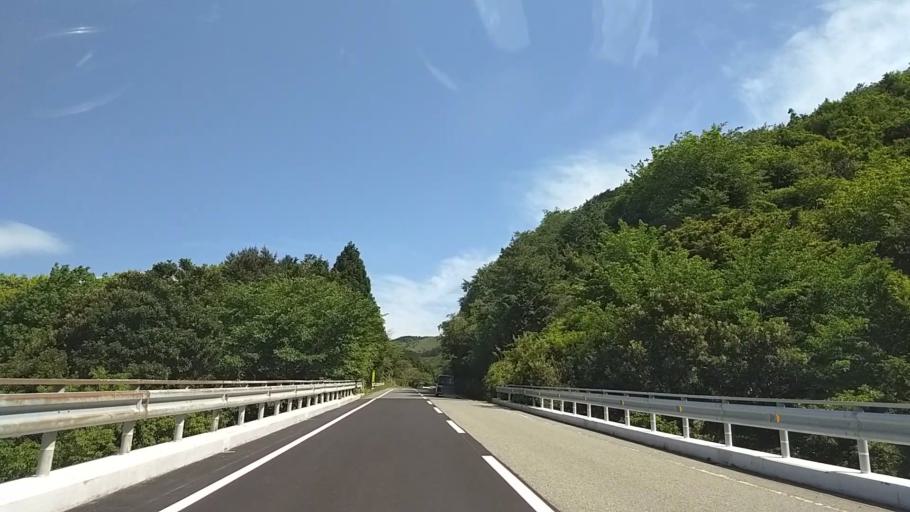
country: JP
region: Shizuoka
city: Atami
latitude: 35.1017
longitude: 139.0268
